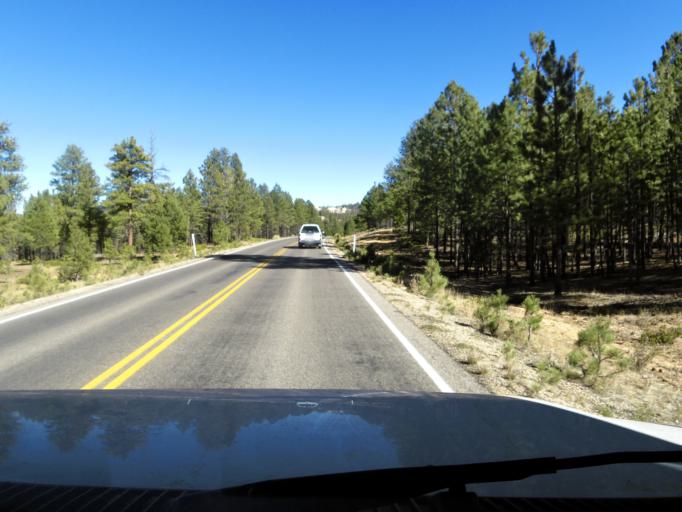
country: US
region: Utah
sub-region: Garfield County
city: Panguitch
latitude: 37.6067
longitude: -112.1988
